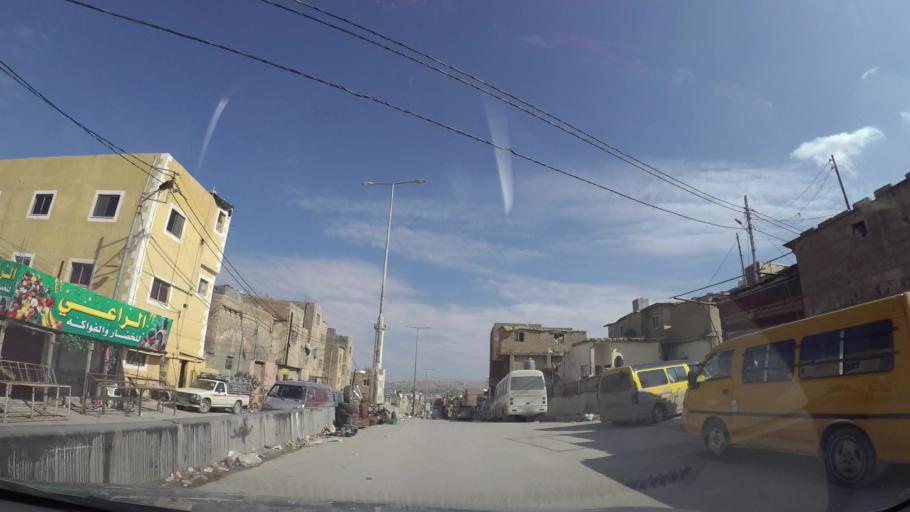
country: JO
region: Amman
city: Al Jubayhah
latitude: 32.0699
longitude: 35.8432
